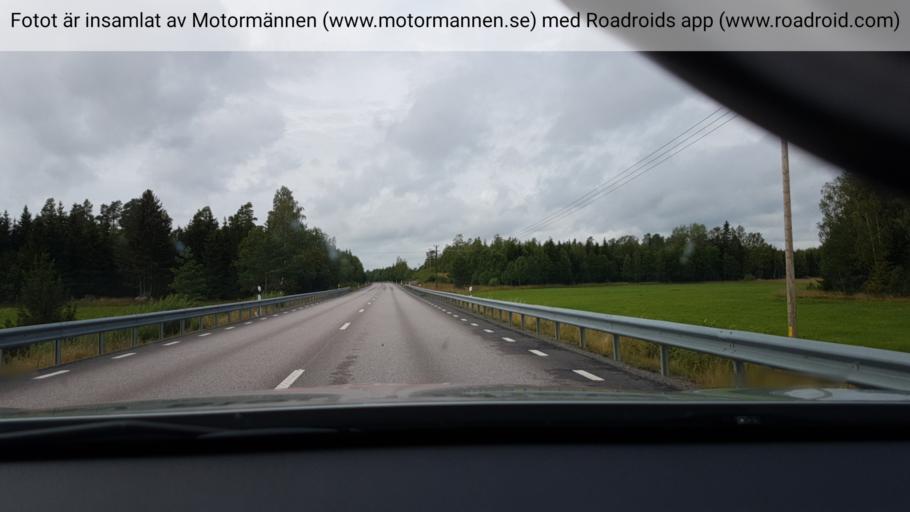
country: SE
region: Uppsala
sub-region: Osthammars Kommun
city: Bjorklinge
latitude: 59.9729
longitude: 17.3620
